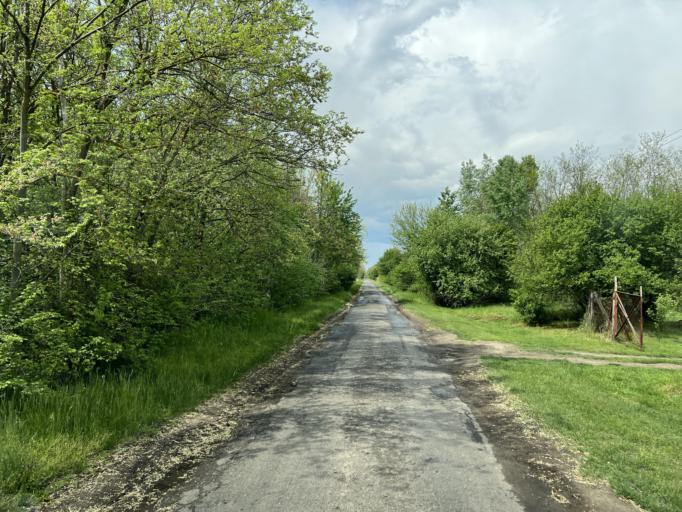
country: HU
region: Pest
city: Nagykoros
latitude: 46.9690
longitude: 19.8191
